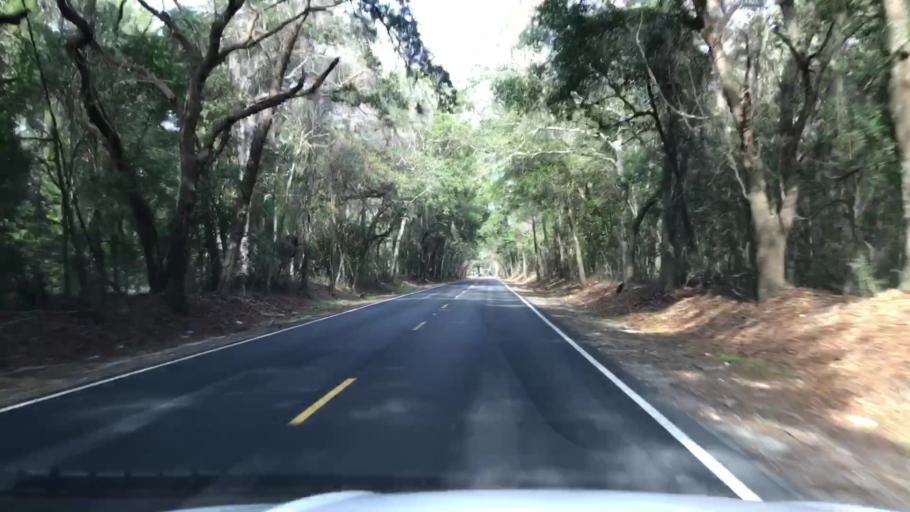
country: US
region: South Carolina
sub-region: Charleston County
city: Folly Beach
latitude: 32.7105
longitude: -80.0179
